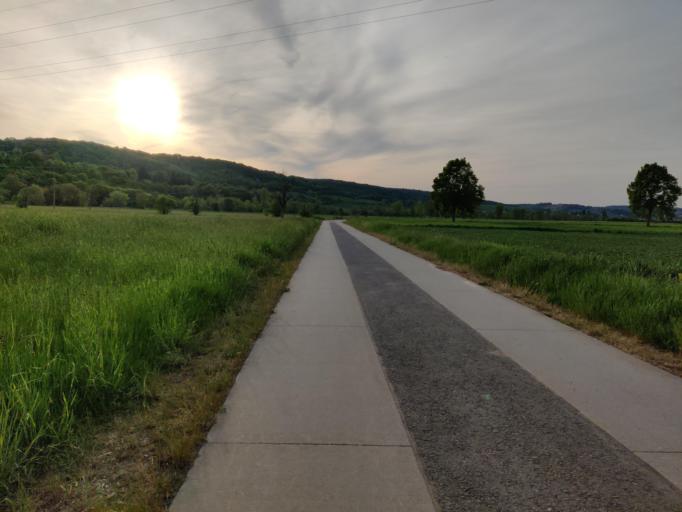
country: DE
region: Saxony-Anhalt
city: Freyburg
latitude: 51.1896
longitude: 11.7836
